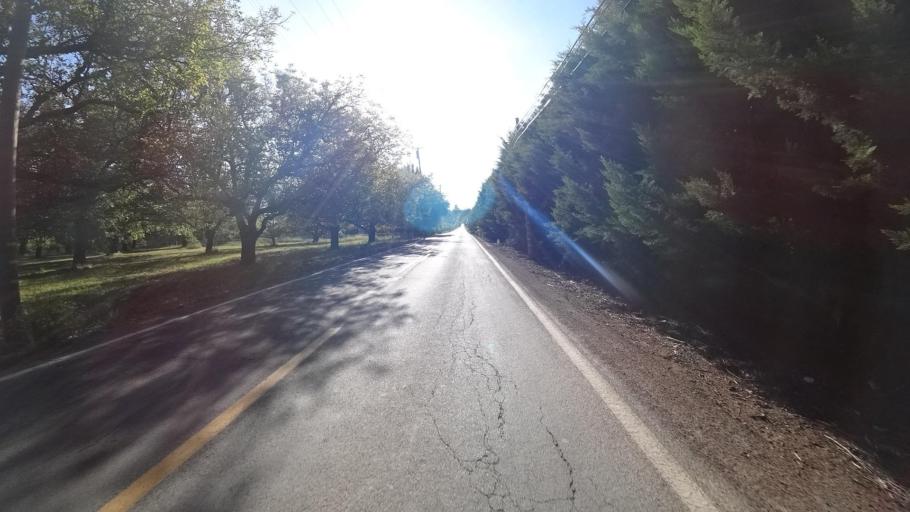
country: US
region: California
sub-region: Lake County
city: Lakeport
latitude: 39.0623
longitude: -122.9429
